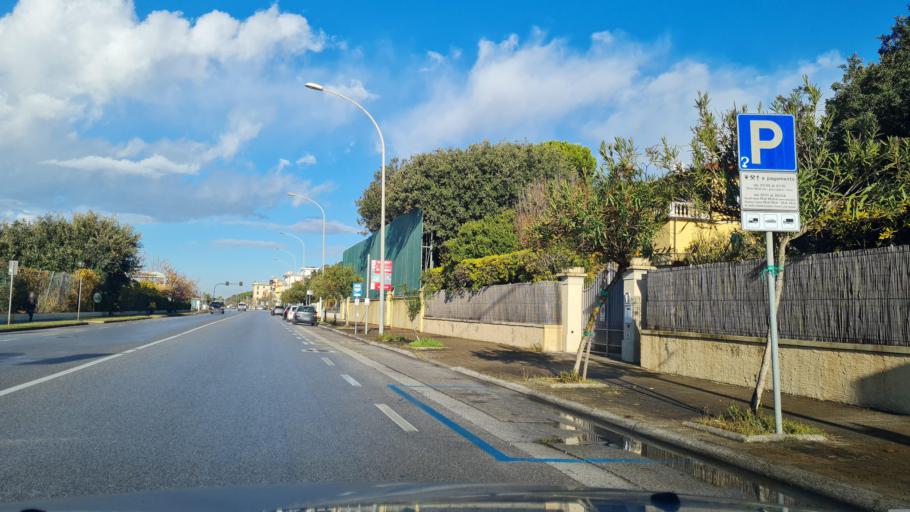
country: IT
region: Tuscany
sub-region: Provincia di Lucca
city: Pietrasanta
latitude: 43.9357
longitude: 10.1913
